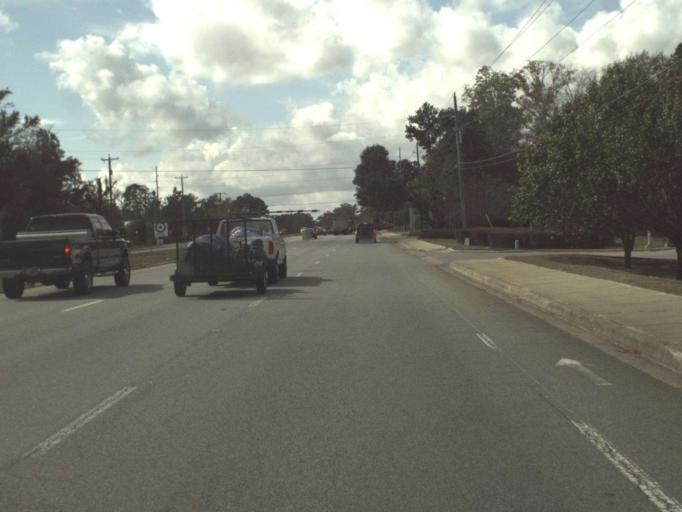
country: US
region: Florida
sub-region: Leon County
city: Tallahassee
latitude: 30.5630
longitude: -84.2159
